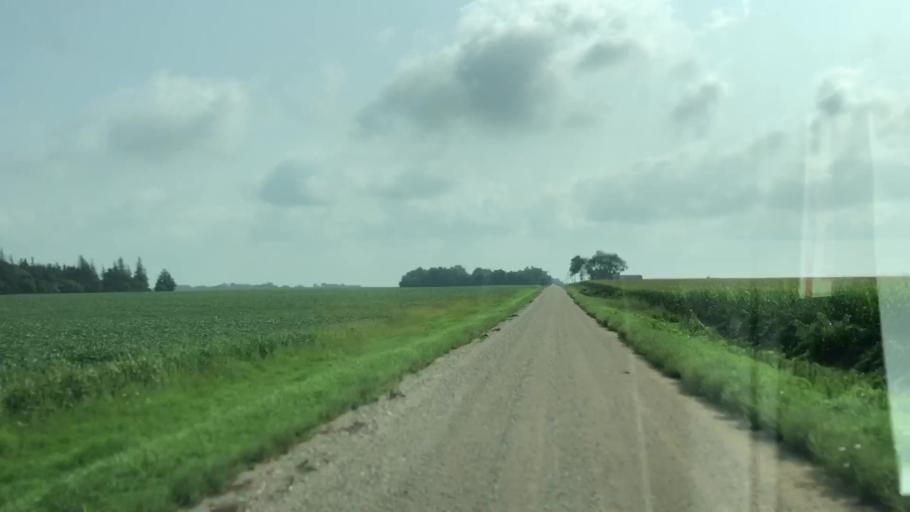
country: US
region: Iowa
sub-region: O'Brien County
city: Sheldon
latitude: 43.2005
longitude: -95.9107
